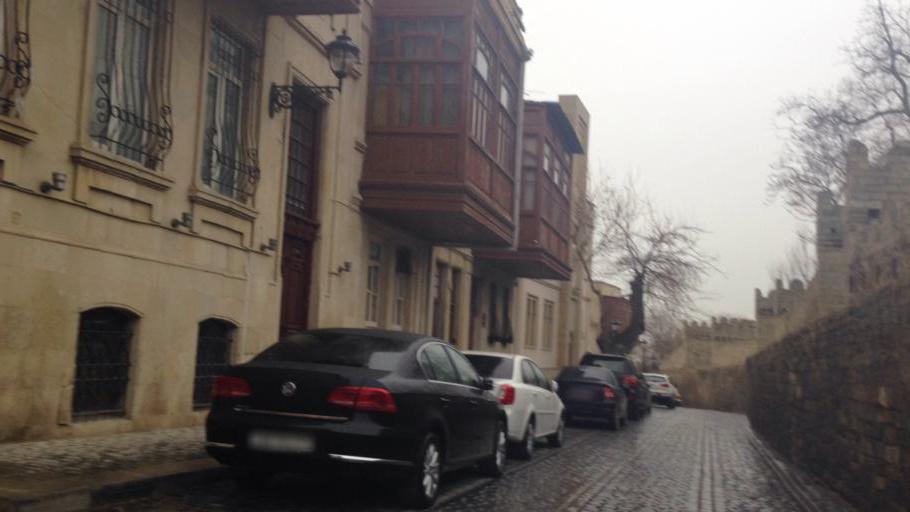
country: AZ
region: Baki
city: Badamdar
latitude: 40.3655
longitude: 49.8322
